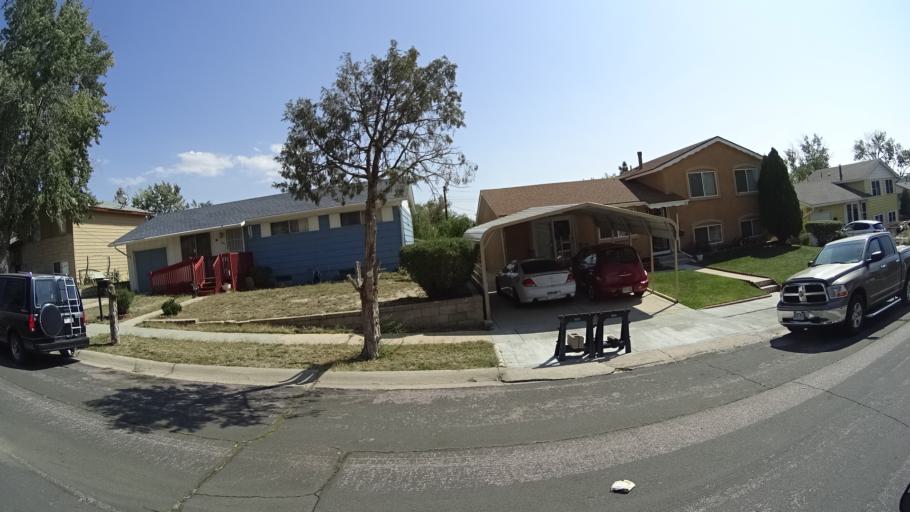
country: US
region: Colorado
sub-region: El Paso County
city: Colorado Springs
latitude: 38.8190
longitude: -104.7826
